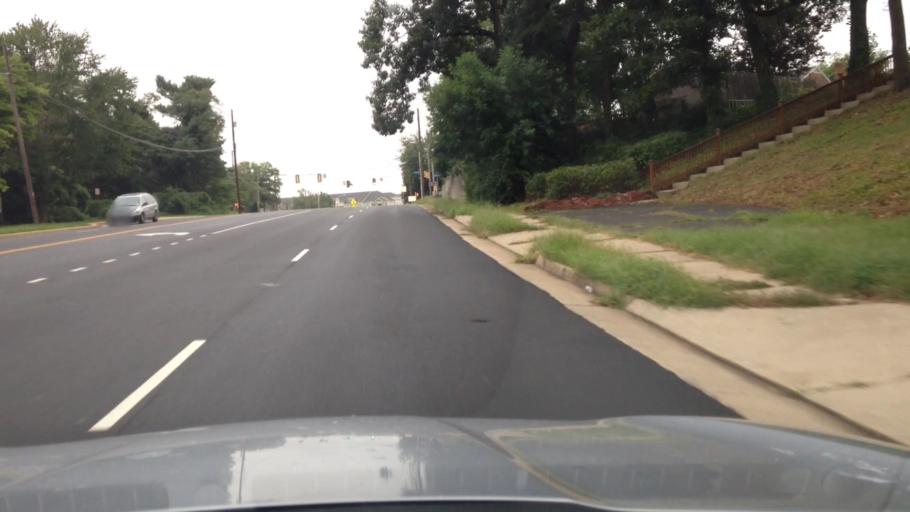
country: US
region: Virginia
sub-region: Fairfax County
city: Huntington
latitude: 38.7939
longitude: -77.0778
